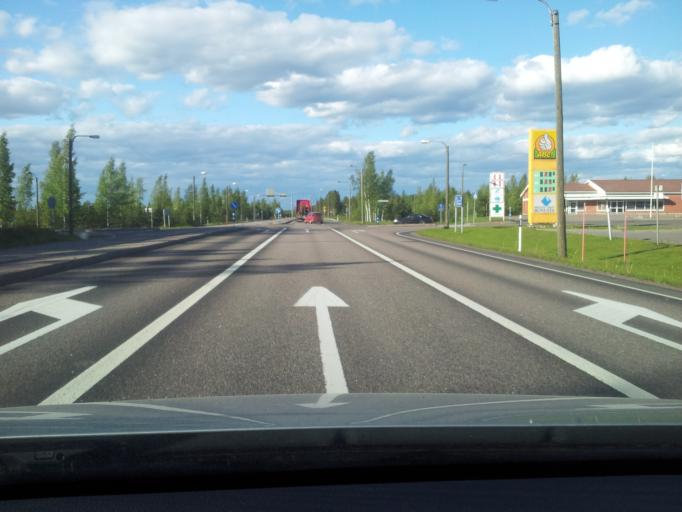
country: FI
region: Kymenlaakso
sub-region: Kouvola
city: Kouvola
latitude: 60.8944
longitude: 26.9101
